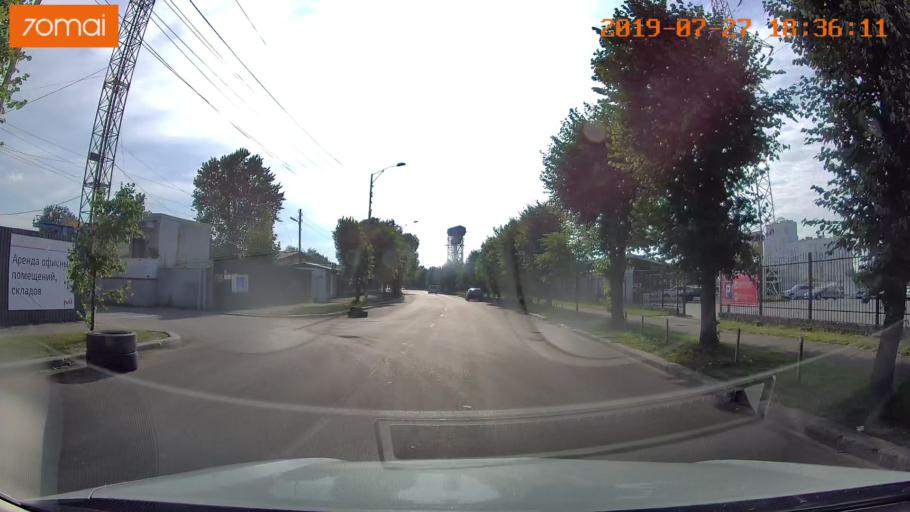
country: RU
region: Kaliningrad
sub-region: Gorod Kaliningrad
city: Kaliningrad
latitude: 54.7052
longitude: 20.4962
